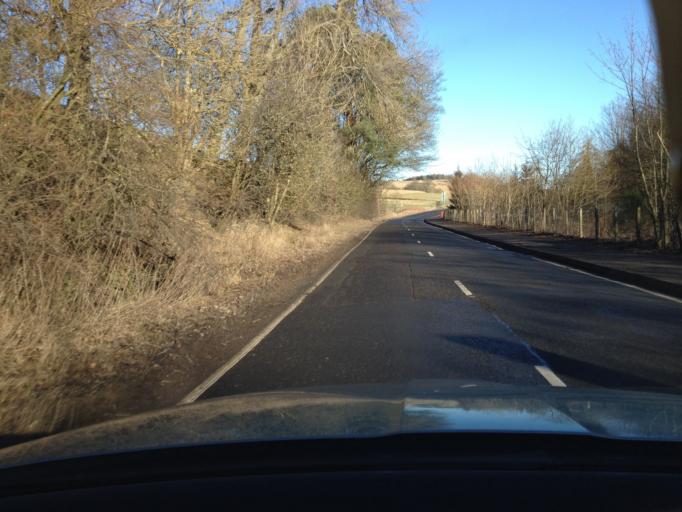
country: GB
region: Scotland
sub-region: Perth and Kinross
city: Milnathort
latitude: 56.2857
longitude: -3.3961
